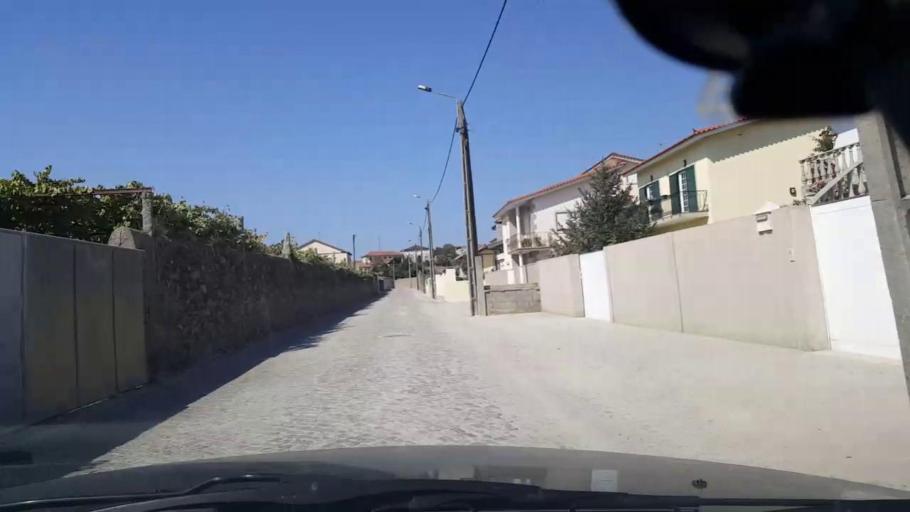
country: PT
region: Porto
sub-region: Povoa de Varzim
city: Pedroso
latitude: 41.3974
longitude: -8.6879
